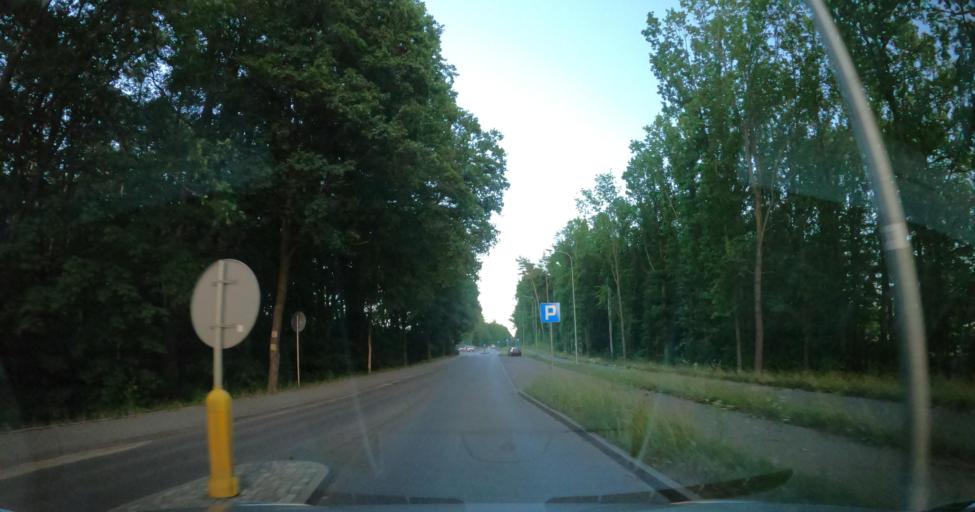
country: PL
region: Pomeranian Voivodeship
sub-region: Powiat leborski
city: Lebork
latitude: 54.5259
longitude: 17.7742
